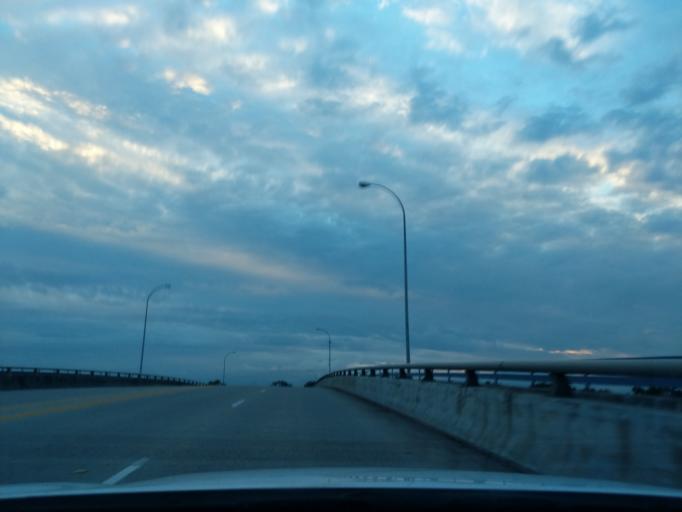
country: US
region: Tennessee
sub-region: Shelby County
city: Memphis
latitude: 35.1582
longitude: -90.0519
